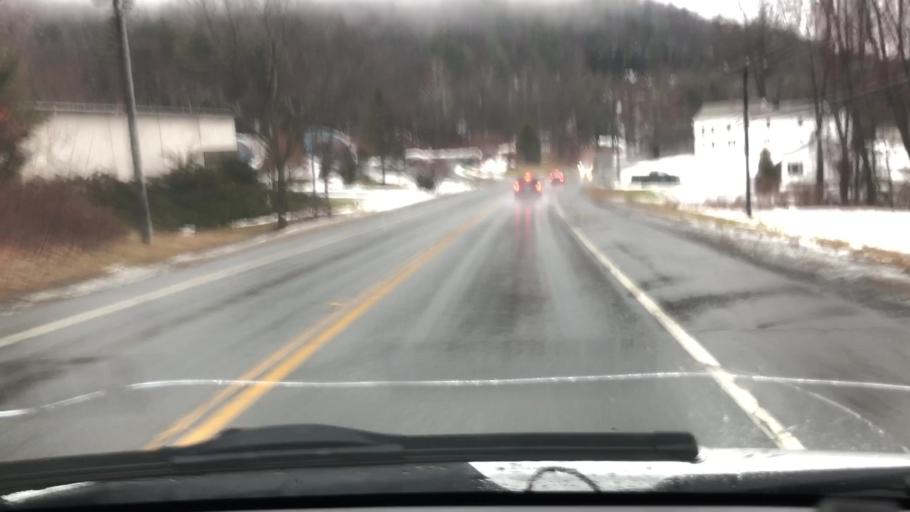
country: US
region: Massachusetts
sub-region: Franklin County
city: Shelburne Falls
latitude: 42.5916
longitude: -72.7212
